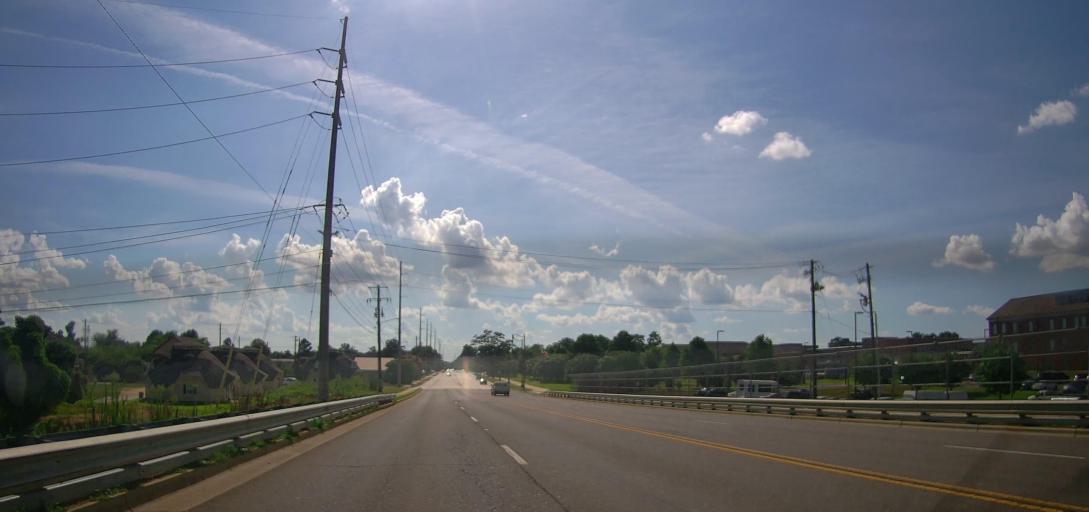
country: US
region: Alabama
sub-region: Tuscaloosa County
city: Holt
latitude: 33.2061
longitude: -87.5134
